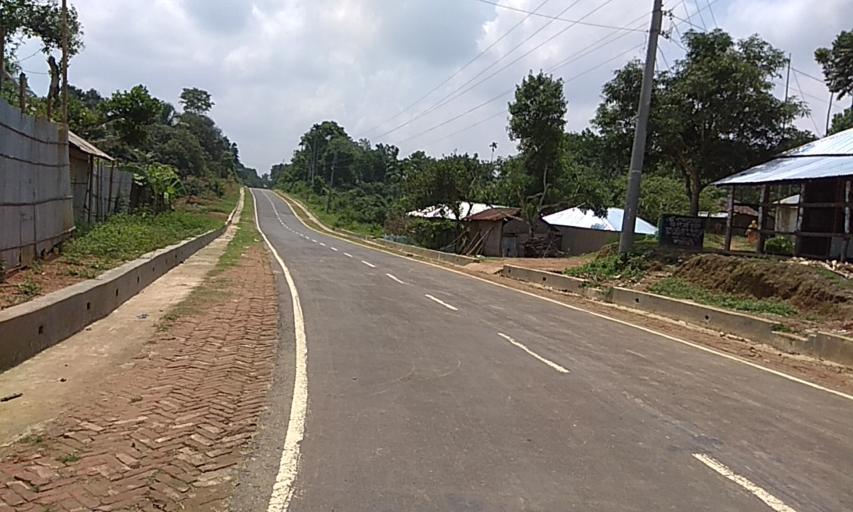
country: BD
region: Chittagong
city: Manikchari
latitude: 22.9384
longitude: 91.8903
